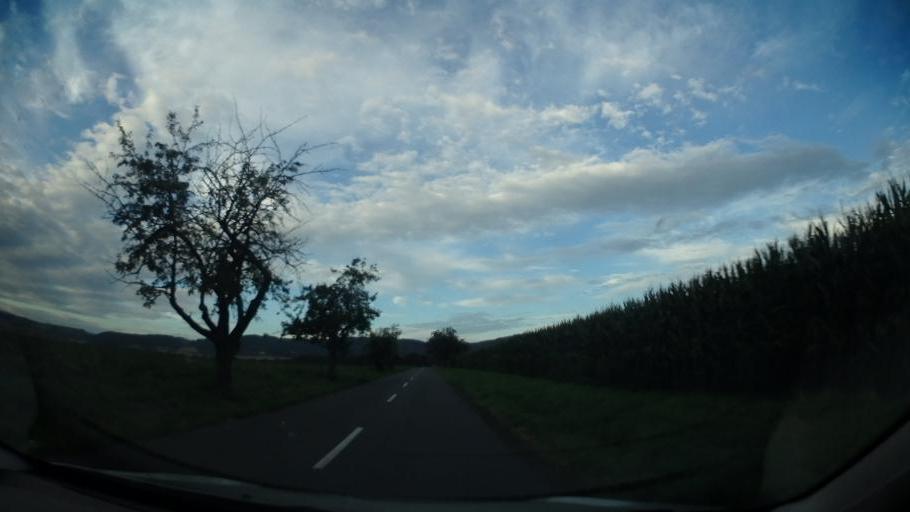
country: CZ
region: Olomoucky
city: Ujezd
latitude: 49.7845
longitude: 17.1840
